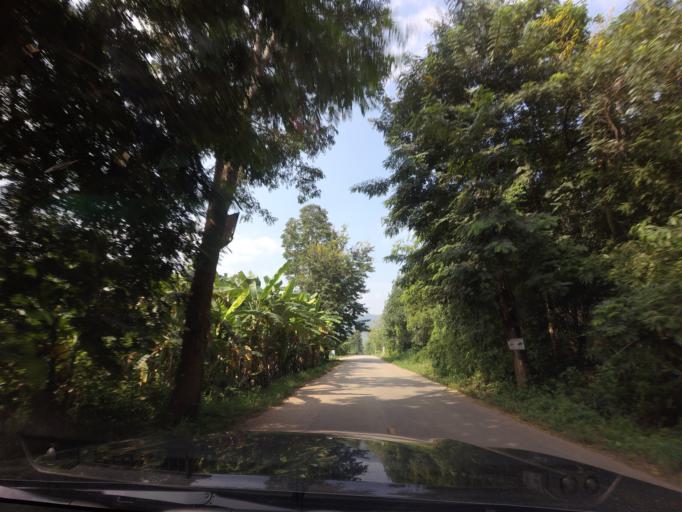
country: TH
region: Loei
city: Chiang Khan
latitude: 17.8169
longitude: 101.5645
